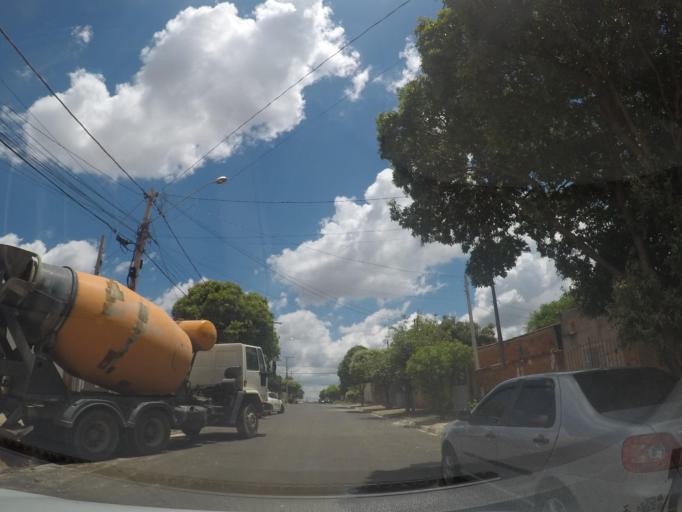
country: BR
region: Sao Paulo
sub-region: Hortolandia
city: Hortolandia
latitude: -22.8196
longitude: -47.2043
